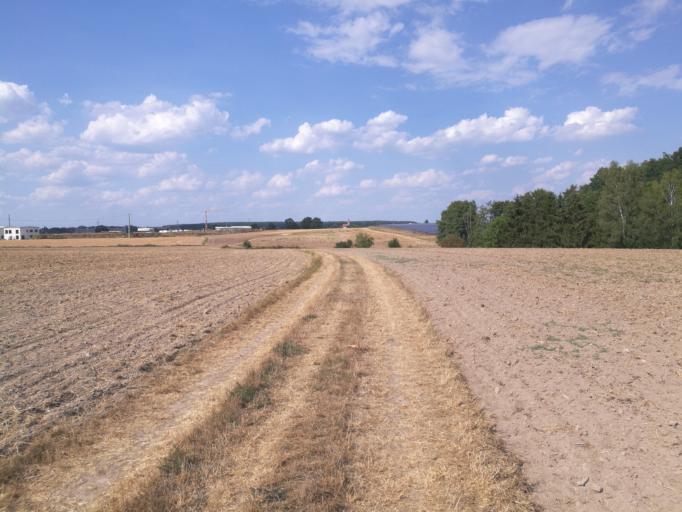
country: DE
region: Bavaria
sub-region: Regierungsbezirk Mittelfranken
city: Veitsbronn
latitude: 49.4987
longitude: 10.8842
